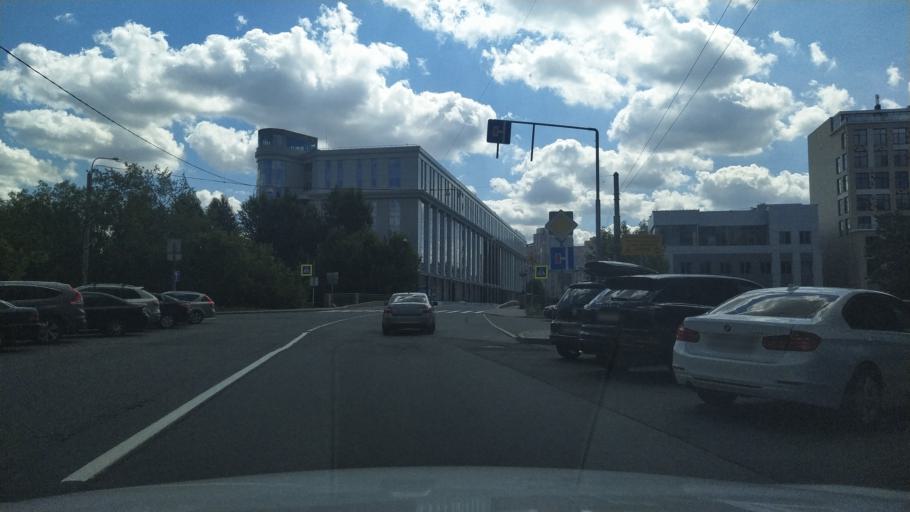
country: RU
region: St.-Petersburg
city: Novaya Derevnya
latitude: 59.9694
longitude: 30.2882
